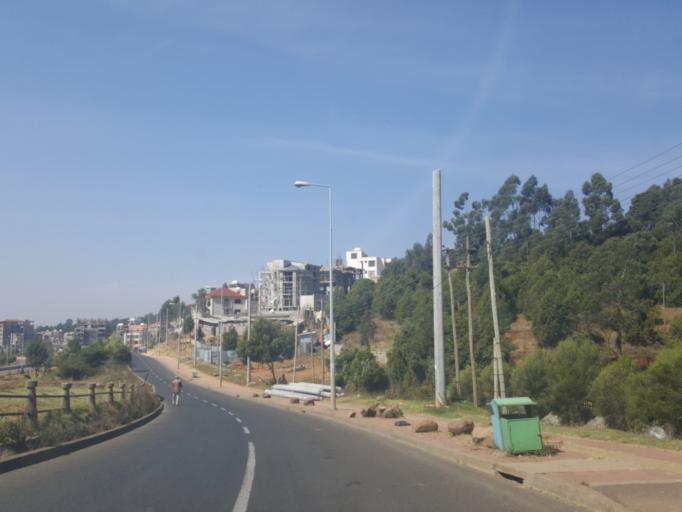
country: ET
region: Adis Abeba
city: Addis Ababa
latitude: 9.0707
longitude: 38.7212
